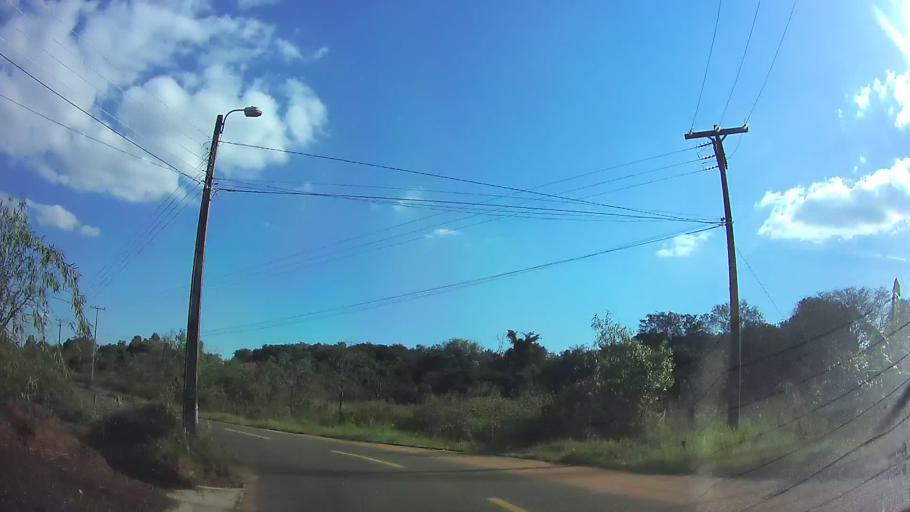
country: PY
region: Central
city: Aregua
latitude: -25.2741
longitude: -57.4449
